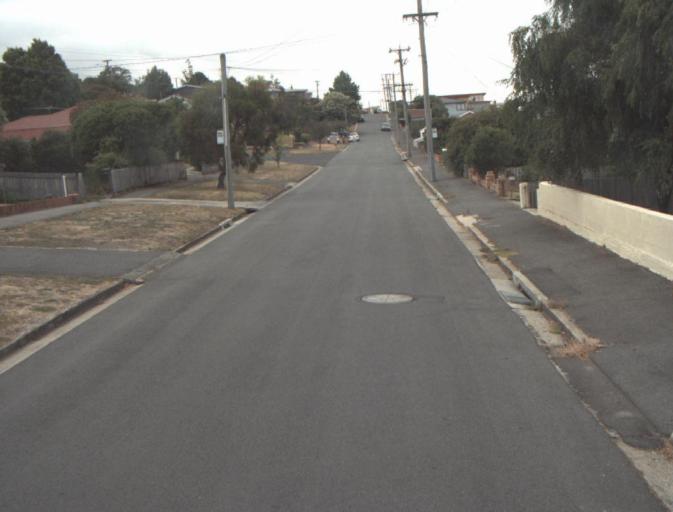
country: AU
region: Tasmania
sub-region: Launceston
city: Summerhill
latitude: -41.4763
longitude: 147.1676
